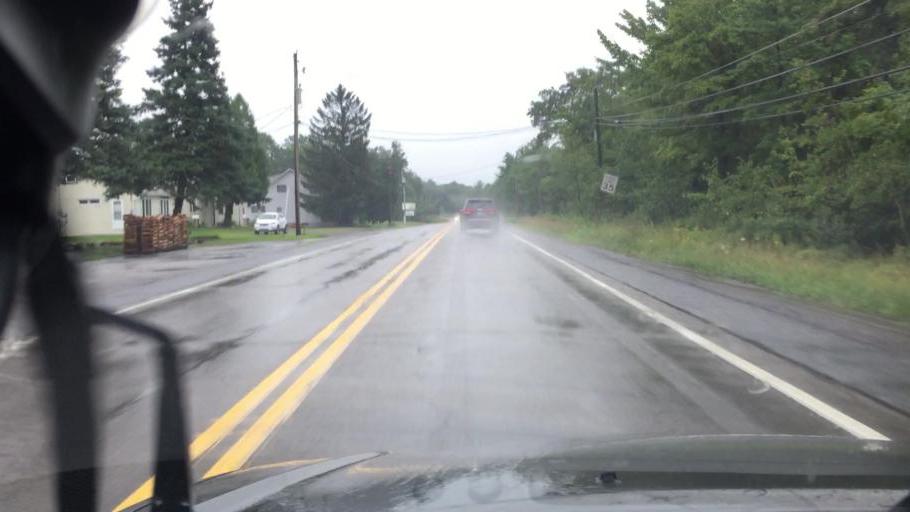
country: US
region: Pennsylvania
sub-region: Luzerne County
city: Freeland
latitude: 41.0175
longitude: -75.8859
